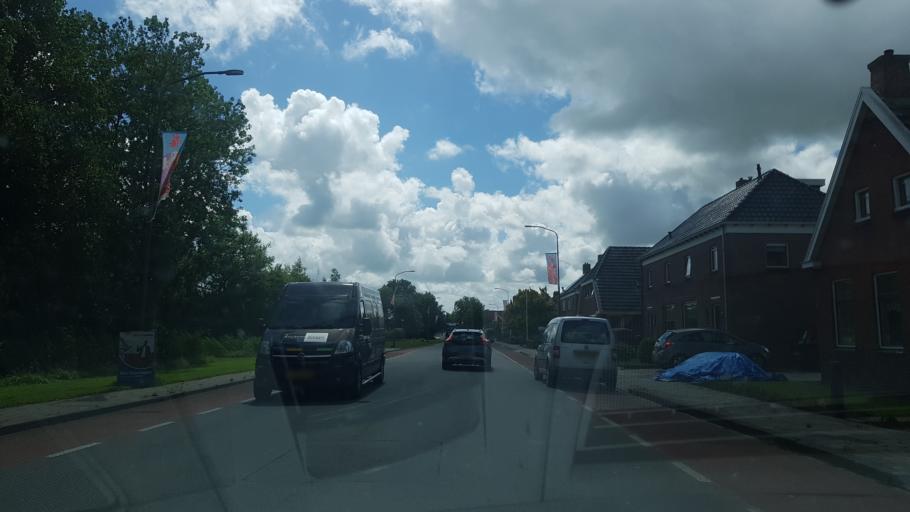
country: NL
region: Groningen
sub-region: Gemeente Winsum
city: Winsum
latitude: 53.3943
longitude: 6.5546
